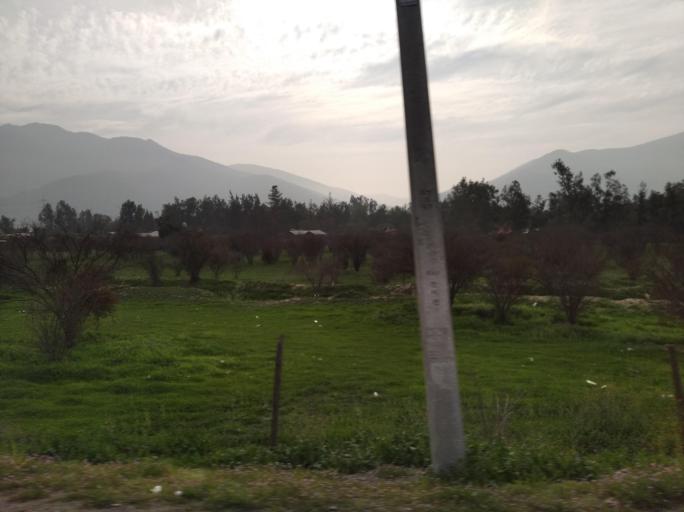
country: CL
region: Santiago Metropolitan
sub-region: Provincia de Chacabuco
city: Lampa
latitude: -33.2680
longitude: -70.8954
